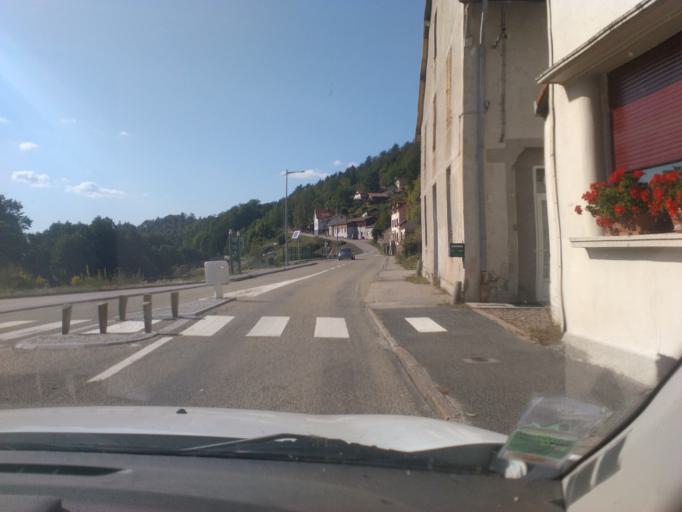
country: FR
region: Lorraine
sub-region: Departement des Vosges
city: Vagney
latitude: 48.0228
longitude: 6.7854
